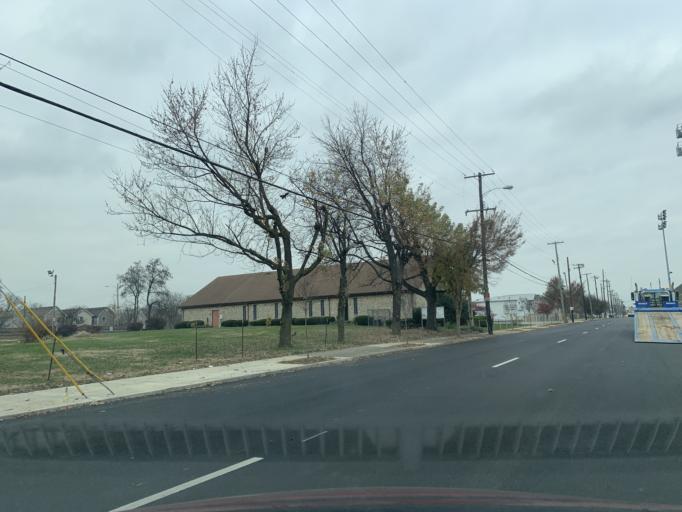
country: US
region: Kentucky
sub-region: Jefferson County
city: Louisville
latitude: 38.2532
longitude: -85.7757
